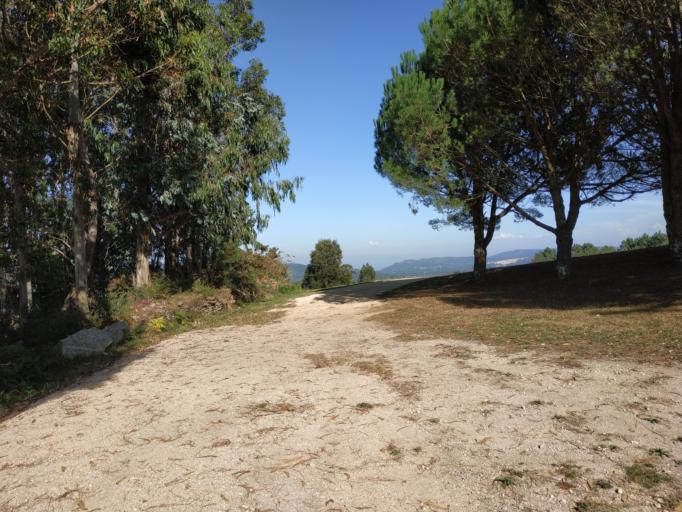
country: ES
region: Galicia
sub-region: Provincia da Coruna
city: Laracha
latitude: 43.2301
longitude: -8.5358
